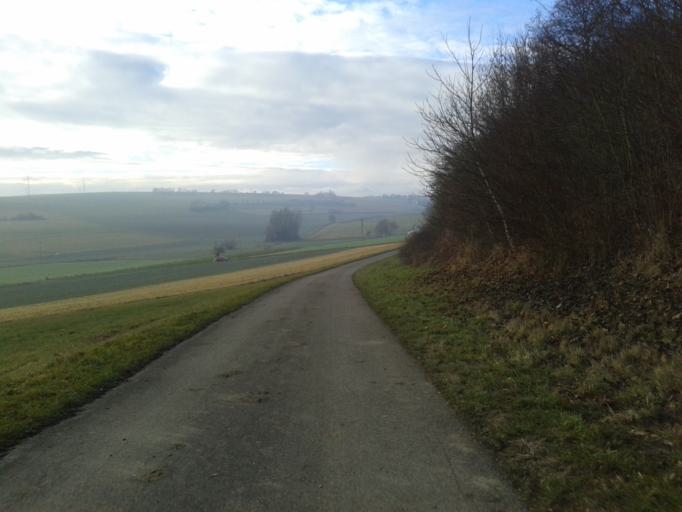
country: DE
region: Baden-Wuerttemberg
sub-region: Tuebingen Region
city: Erbach
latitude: 48.3893
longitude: 9.9154
